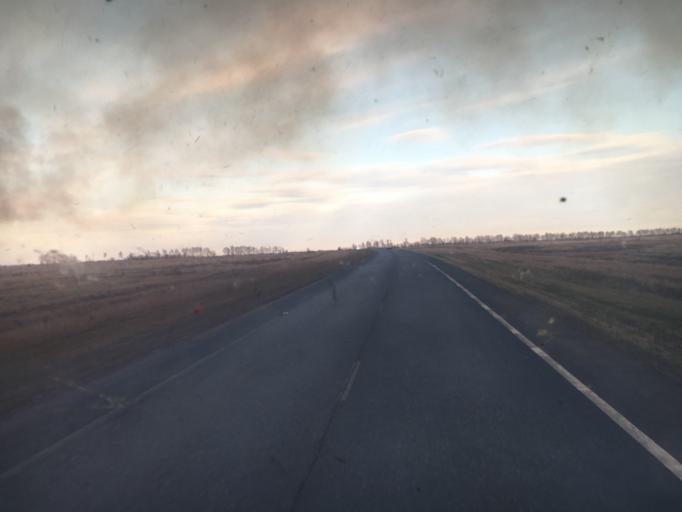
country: RU
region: Samara
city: Borskoye
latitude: 52.7690
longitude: 51.6150
